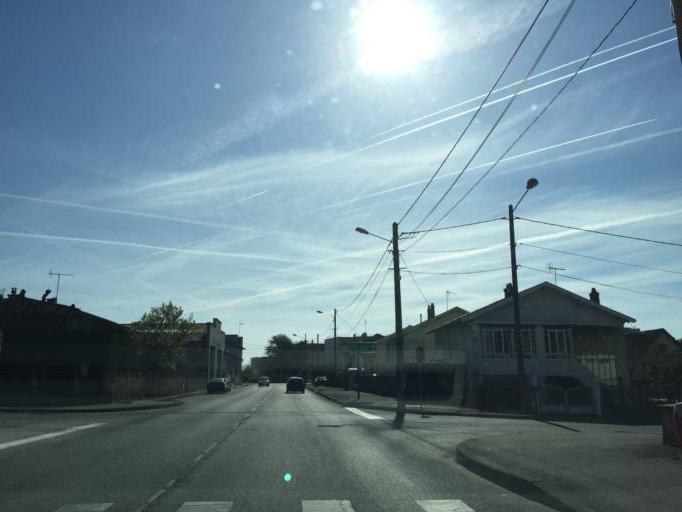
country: FR
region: Rhone-Alpes
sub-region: Departement de la Loire
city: Feurs
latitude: 45.7364
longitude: 4.2232
